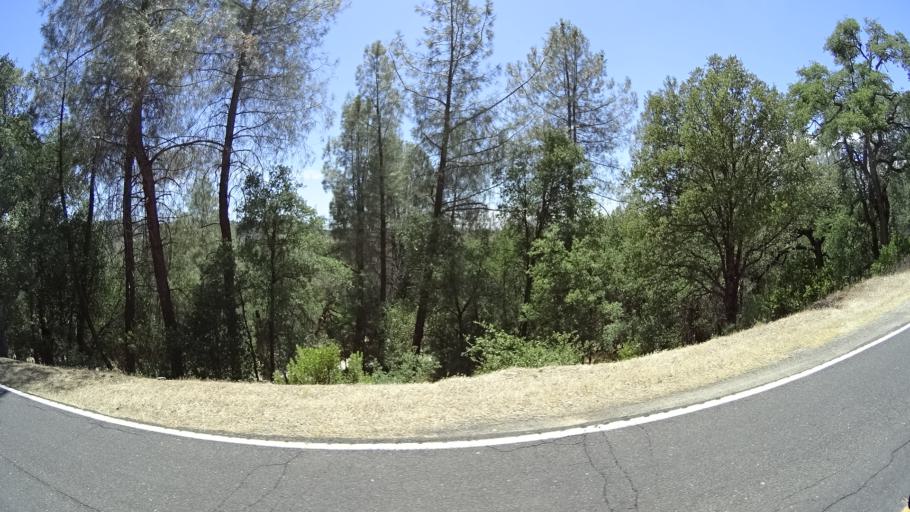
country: US
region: California
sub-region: Calaveras County
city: Mountain Ranch
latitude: 38.2199
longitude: -120.4805
